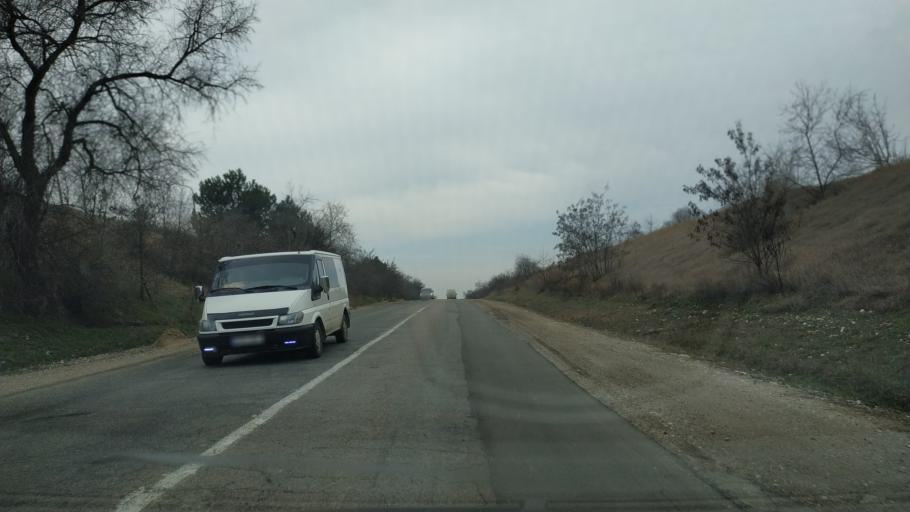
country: MD
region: Cahul
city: Cahul
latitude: 45.9581
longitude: 28.3719
